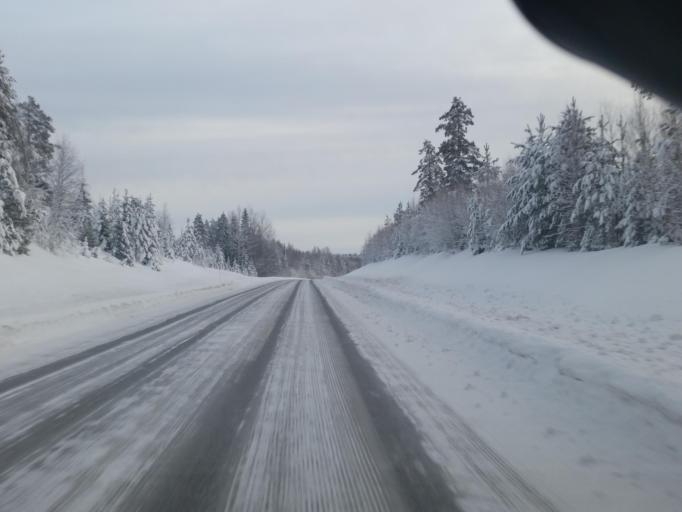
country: SE
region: Norrbotten
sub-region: Pitea Kommun
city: Norrfjarden
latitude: 65.6422
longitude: 21.3214
